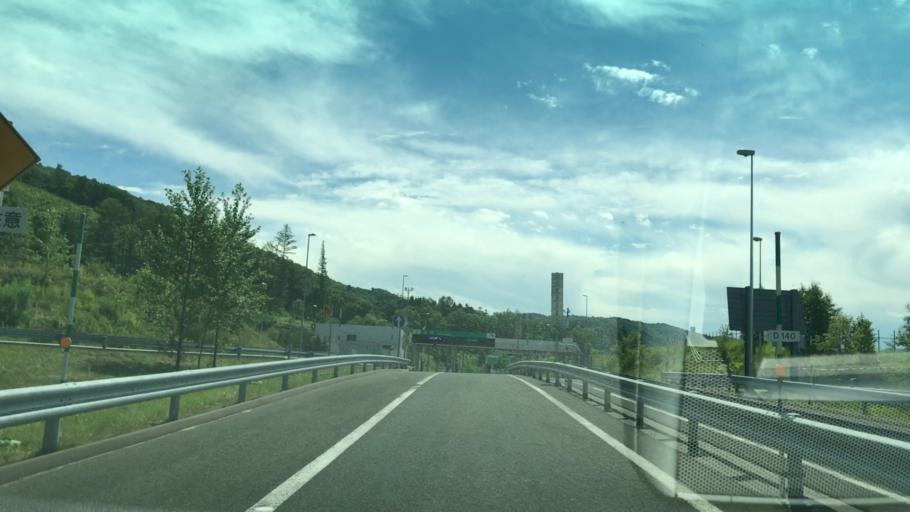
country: JP
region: Hokkaido
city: Shimo-furano
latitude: 42.9795
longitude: 142.4096
